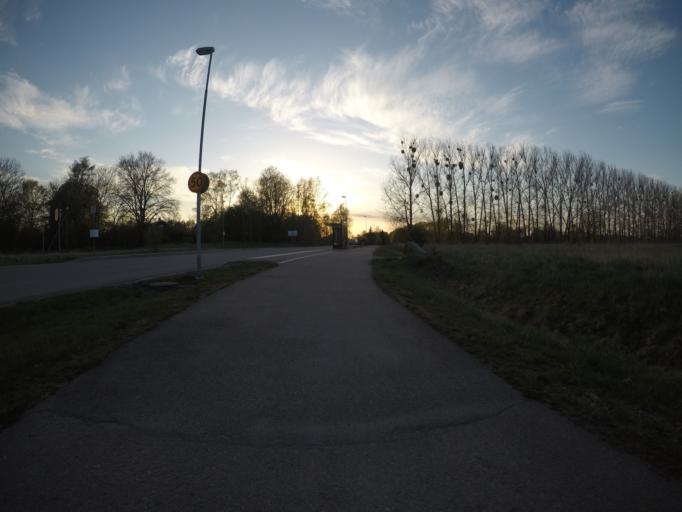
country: SE
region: Vaestmanland
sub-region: Vasteras
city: Vasteras
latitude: 59.5932
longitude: 16.6135
